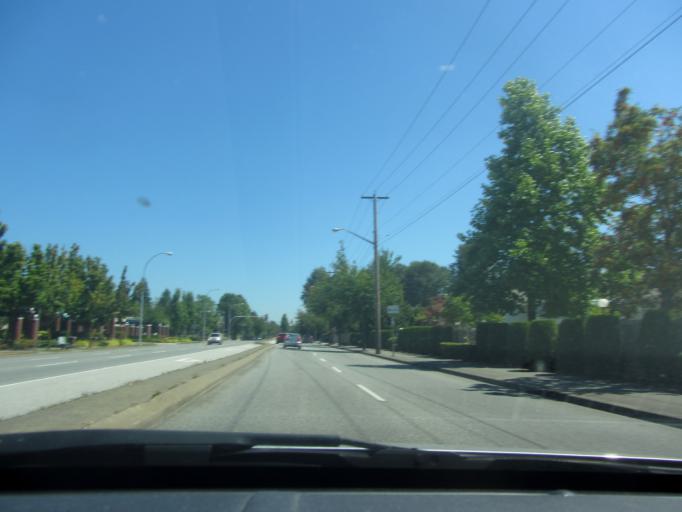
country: CA
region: British Columbia
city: Delta
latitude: 49.1340
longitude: -122.8873
